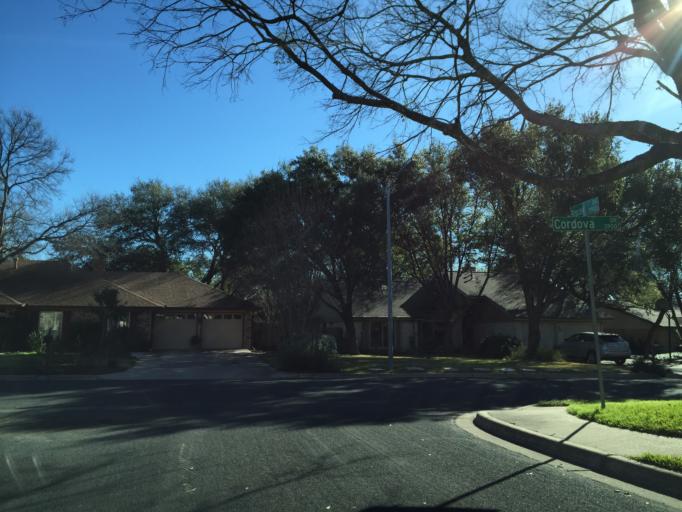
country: US
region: Texas
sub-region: Williamson County
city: Jollyville
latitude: 30.4036
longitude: -97.7323
